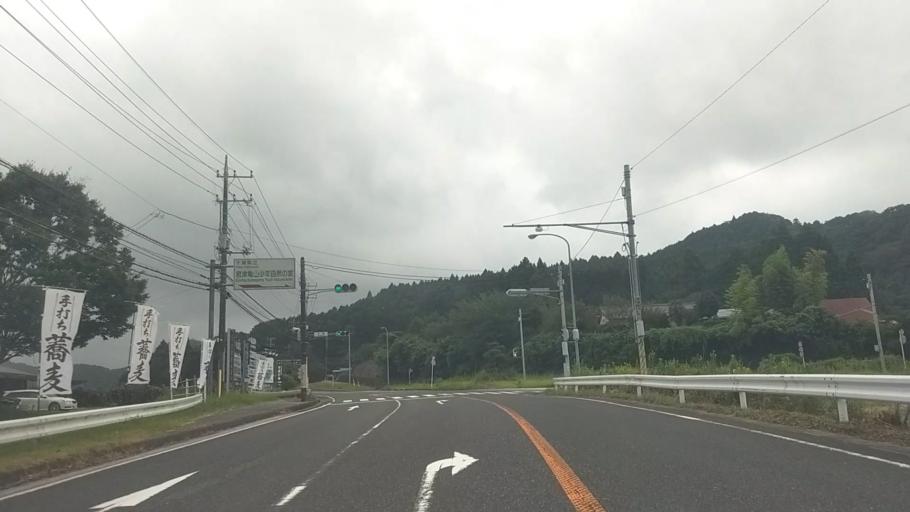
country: JP
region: Chiba
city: Kawaguchi
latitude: 35.2057
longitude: 140.0710
